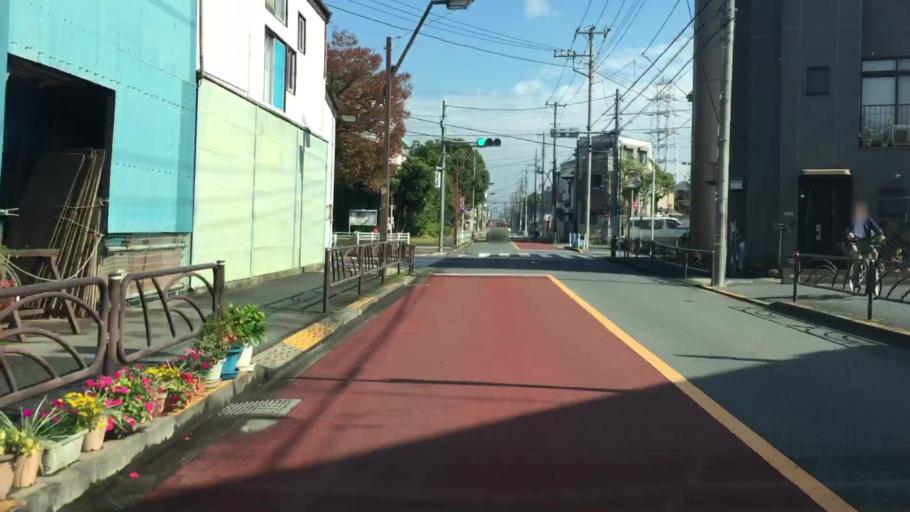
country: JP
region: Saitama
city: Yashio-shi
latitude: 35.7584
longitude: 139.8321
